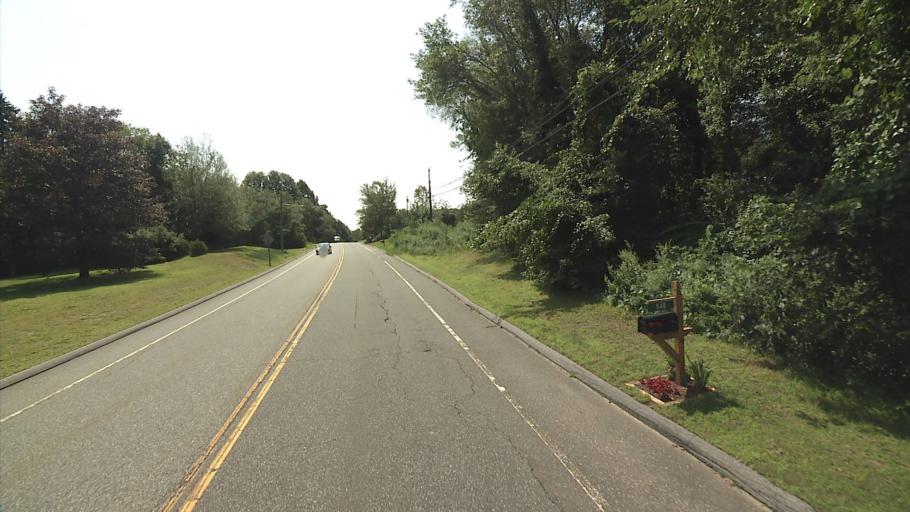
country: US
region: Connecticut
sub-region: New London County
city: Colchester
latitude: 41.5169
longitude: -72.2539
